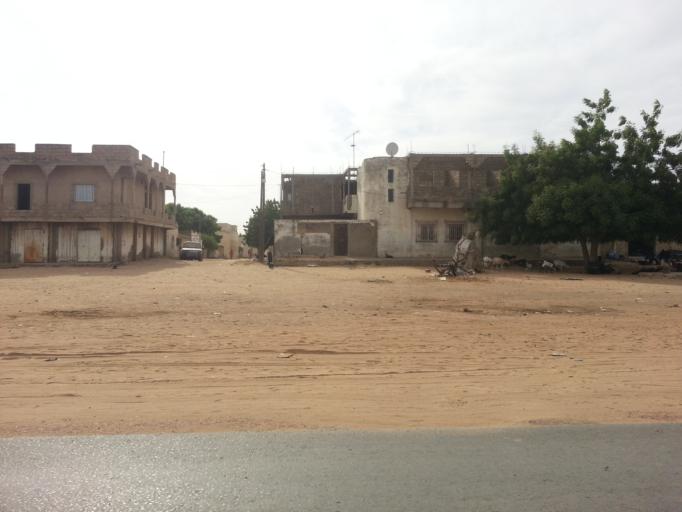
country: SN
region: Diourbel
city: Touba
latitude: 14.8637
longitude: -15.8604
